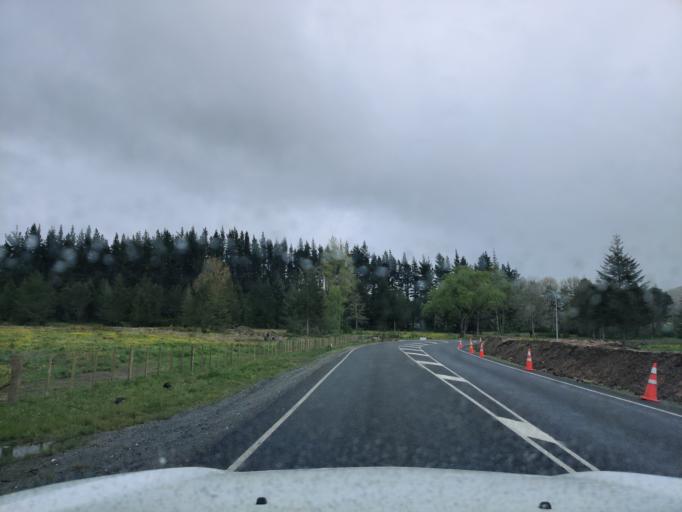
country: NZ
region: Bay of Plenty
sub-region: Rotorua District
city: Rotorua
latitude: -38.1770
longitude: 176.2524
